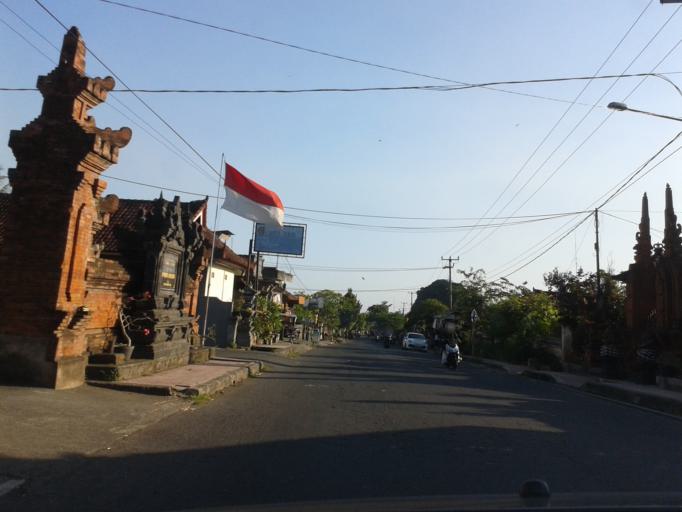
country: ID
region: Bali
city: Klungkung
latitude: -8.5142
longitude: 115.4015
